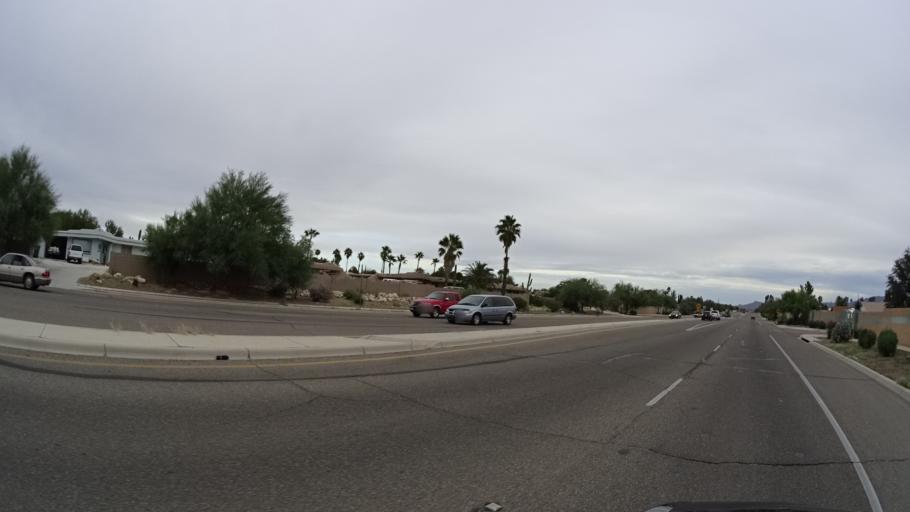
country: US
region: Arizona
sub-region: Pima County
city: Casas Adobes
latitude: 32.3499
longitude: -111.0471
